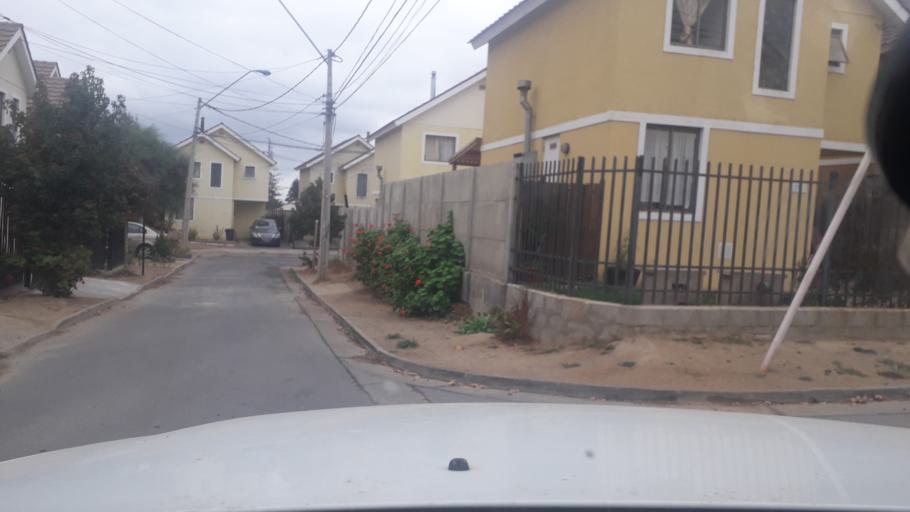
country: CL
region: Valparaiso
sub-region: Provincia de Marga Marga
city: Villa Alemana
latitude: -33.0517
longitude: -71.3362
